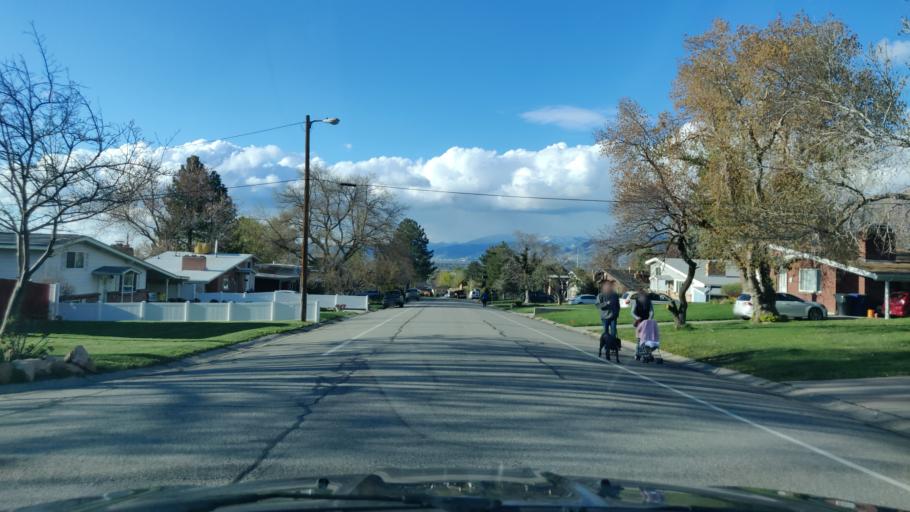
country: US
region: Utah
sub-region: Salt Lake County
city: Little Cottonwood Creek Valley
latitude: 40.6207
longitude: -111.8283
